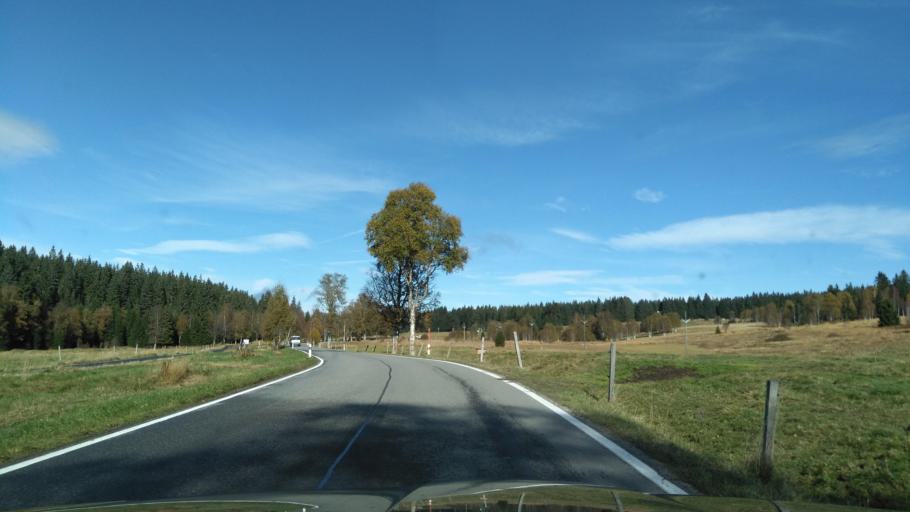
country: CZ
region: Jihocesky
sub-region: Okres Prachatice
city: Borova Lada
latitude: 49.0237
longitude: 13.5809
